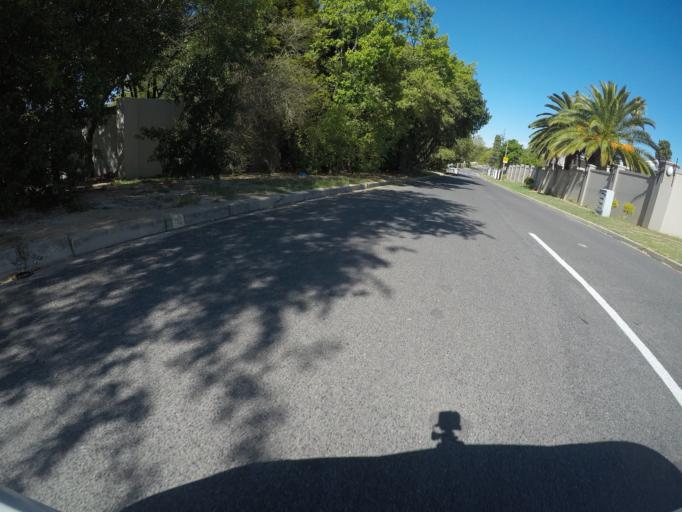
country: ZA
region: Western Cape
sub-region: City of Cape Town
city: Kraaifontein
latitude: -33.8595
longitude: 18.6470
